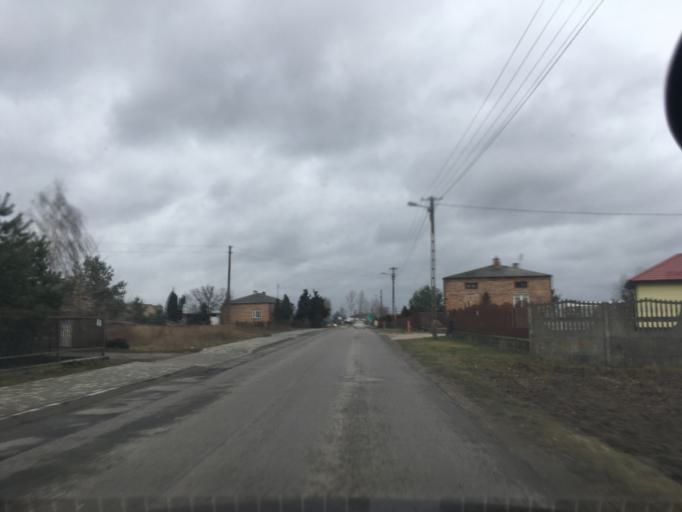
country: PL
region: Masovian Voivodeship
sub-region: Powiat piaseczynski
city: Lesznowola
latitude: 52.1200
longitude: 20.9302
